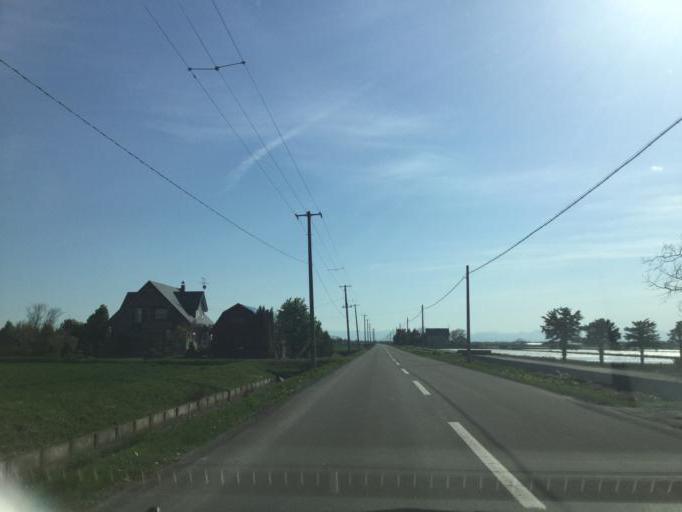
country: JP
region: Hokkaido
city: Iwamizawa
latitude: 43.1662
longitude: 141.7335
